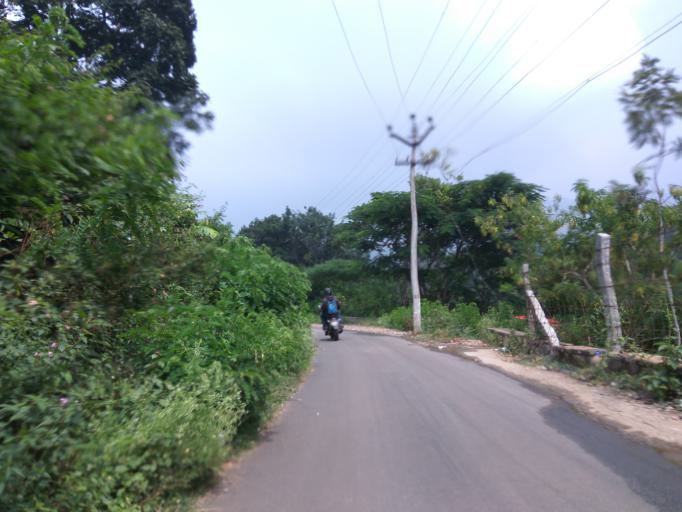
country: IN
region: Tamil Nadu
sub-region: Salem
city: Salem
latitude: 11.7892
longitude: 78.2018
